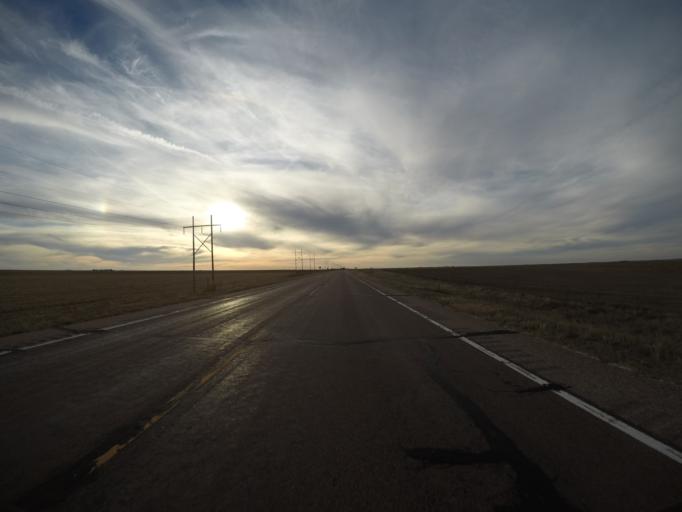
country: US
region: Colorado
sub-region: Yuma County
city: Yuma
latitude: 39.6551
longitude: -102.7994
